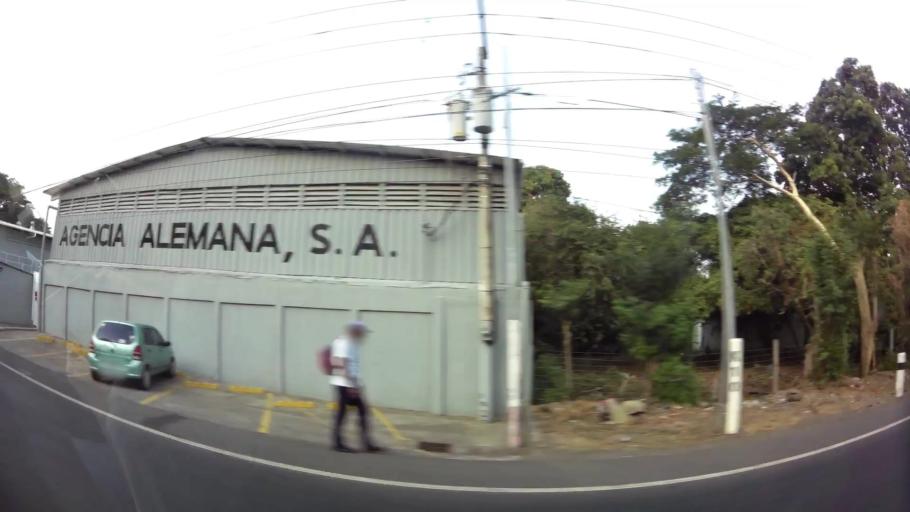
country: NI
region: Managua
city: Ciudad Sandino
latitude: 12.1474
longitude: -86.3358
